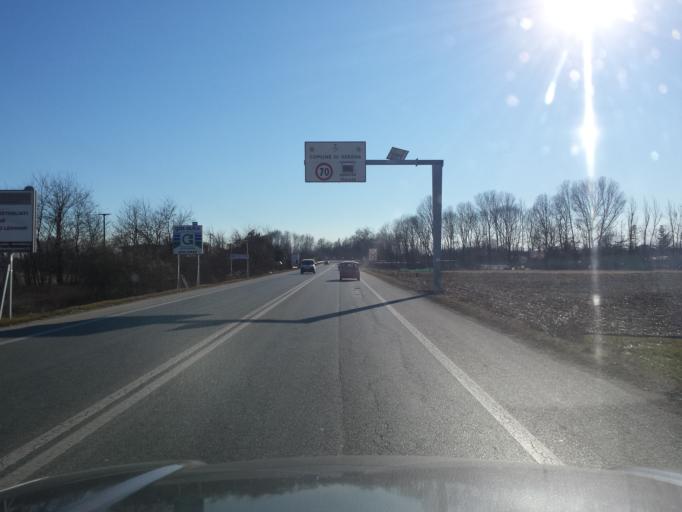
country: IT
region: Piedmont
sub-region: Provincia di Torino
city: Ozegna
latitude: 45.3414
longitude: 7.7406
